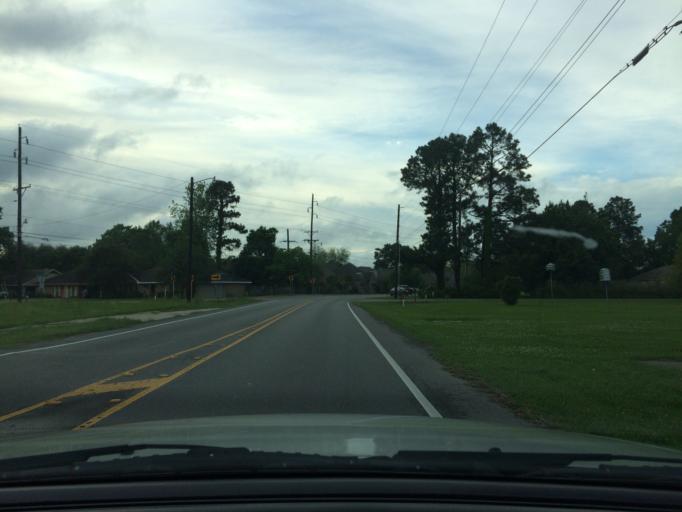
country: US
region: Louisiana
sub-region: Lafayette Parish
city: Scott
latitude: 30.2153
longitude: -92.0640
